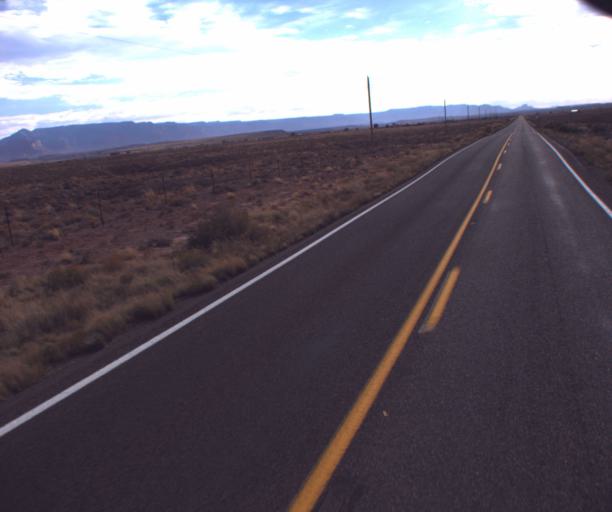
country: US
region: Arizona
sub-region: Apache County
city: Many Farms
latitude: 36.5247
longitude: -109.4975
